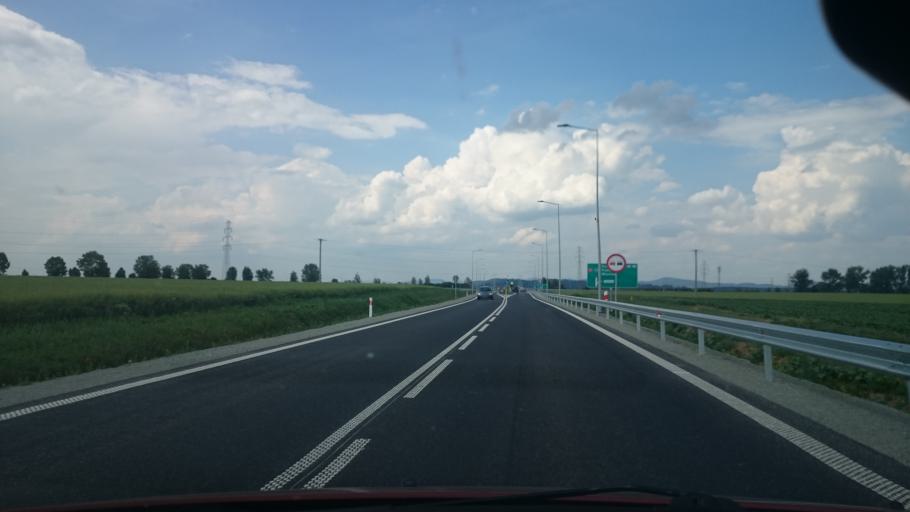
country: PL
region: Lower Silesian Voivodeship
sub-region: Powiat klodzki
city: Klodzko
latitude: 50.4325
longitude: 16.6286
